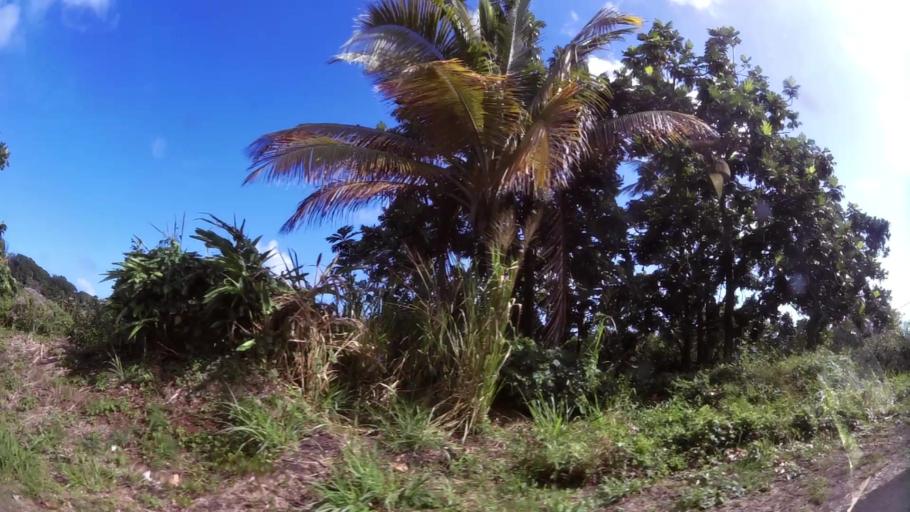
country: DM
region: Saint Andrew
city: Marigot
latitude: 15.5074
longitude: -61.2629
